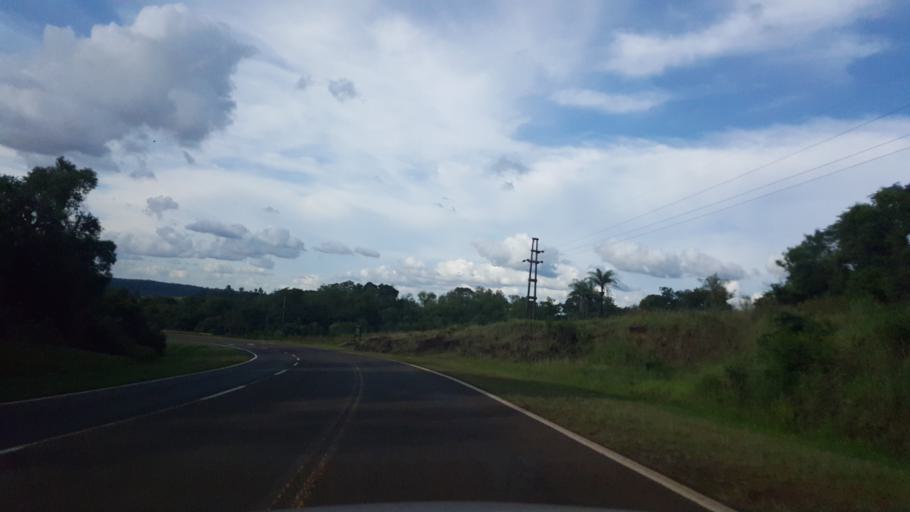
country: AR
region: Misiones
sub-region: Departamento de Candelaria
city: Loreto
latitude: -27.3296
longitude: -55.5418
